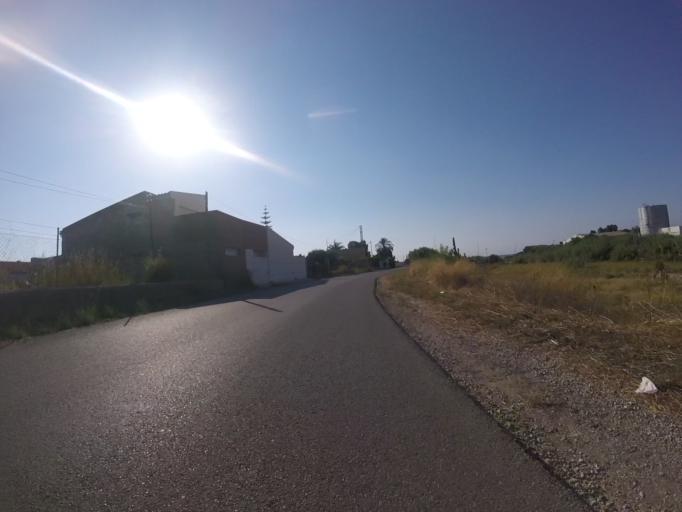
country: ES
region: Valencia
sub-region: Provincia de Castello
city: Benicarlo
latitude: 40.4241
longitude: 0.4333
